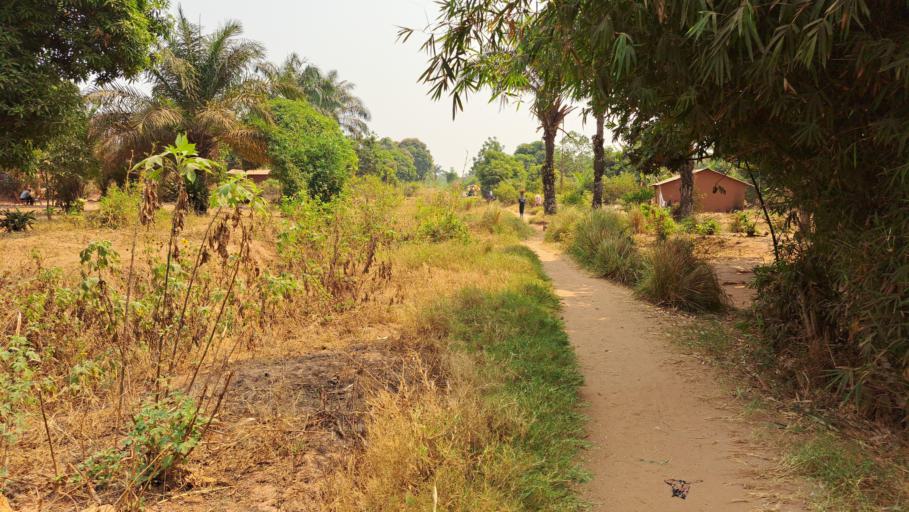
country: CD
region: Kasai-Oriental
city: Mbuji-Mayi
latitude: -6.0987
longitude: 23.5647
